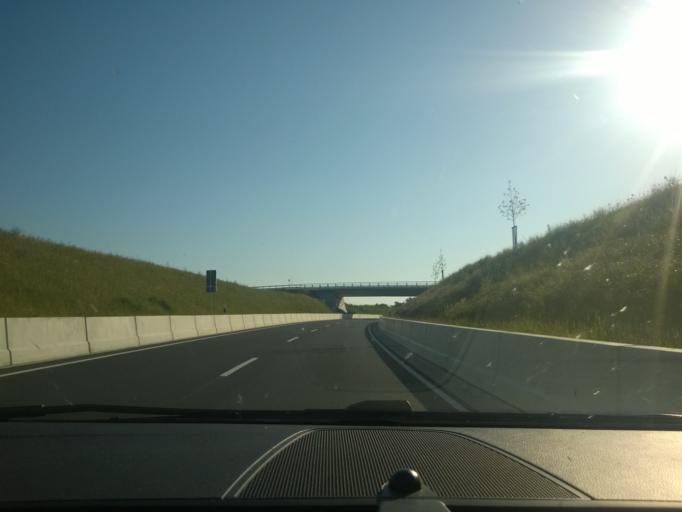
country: DE
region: North Rhine-Westphalia
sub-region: Regierungsbezirk Munster
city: Nottuln
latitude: 51.9377
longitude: 7.3525
